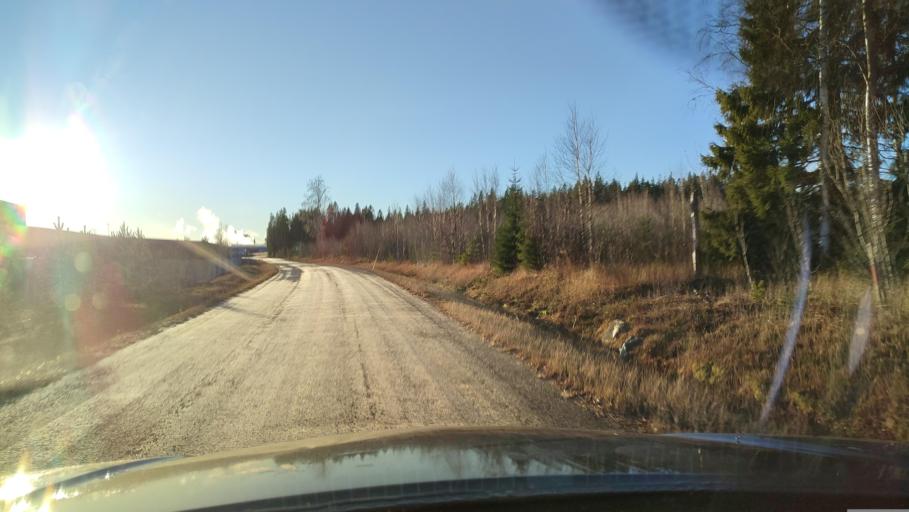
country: SE
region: Vaesterbotten
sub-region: Skelleftea Kommun
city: Viken
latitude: 64.7093
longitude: 20.9053
